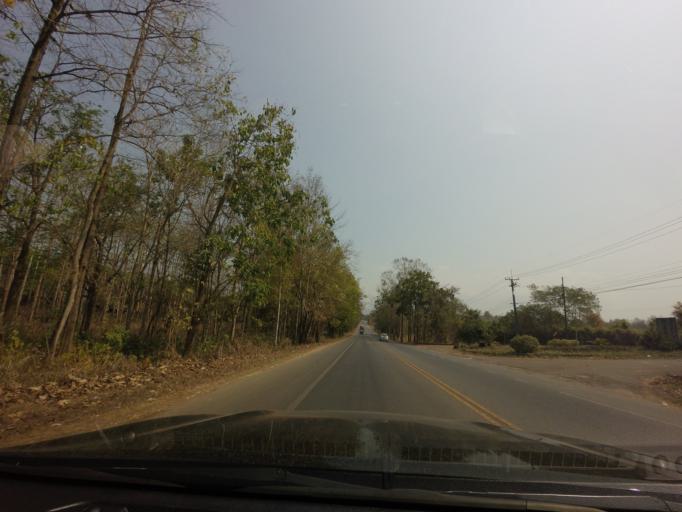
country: TH
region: Kanchanaburi
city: Thong Pha Phum
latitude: 14.6406
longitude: 98.6892
